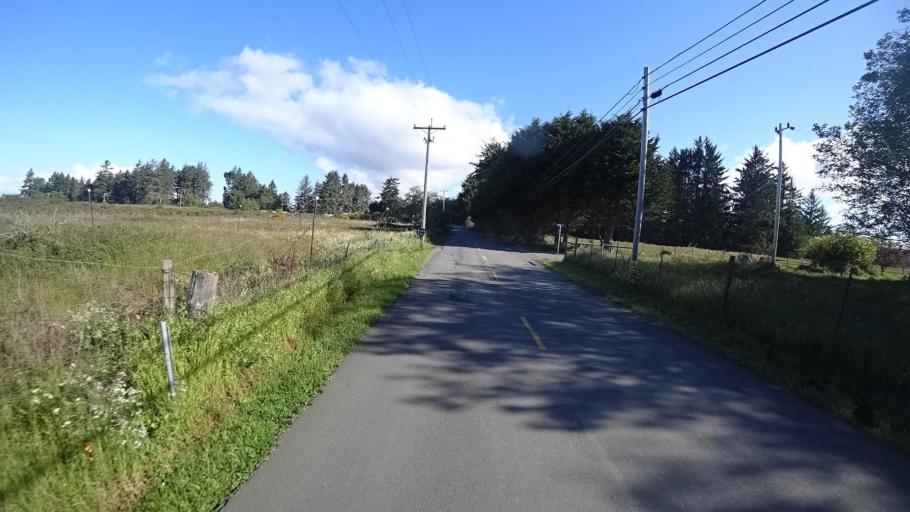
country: US
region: California
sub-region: Humboldt County
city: Westhaven-Moonstone
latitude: 41.0033
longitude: -124.1006
